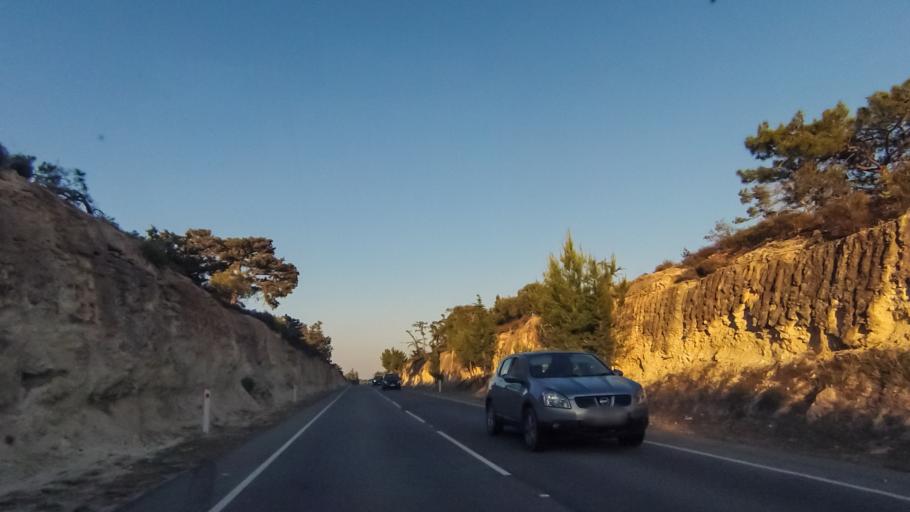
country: CY
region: Limassol
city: Sotira
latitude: 34.6706
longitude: 32.8699
